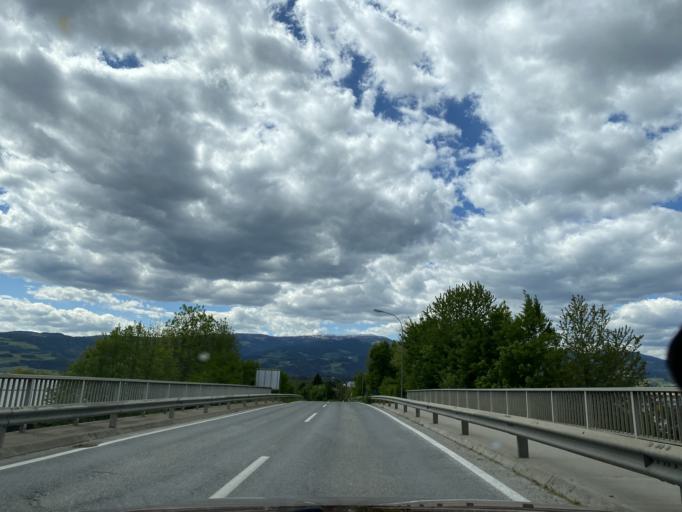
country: AT
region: Carinthia
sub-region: Politischer Bezirk Wolfsberg
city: Wolfsberg
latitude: 46.8182
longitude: 14.8484
